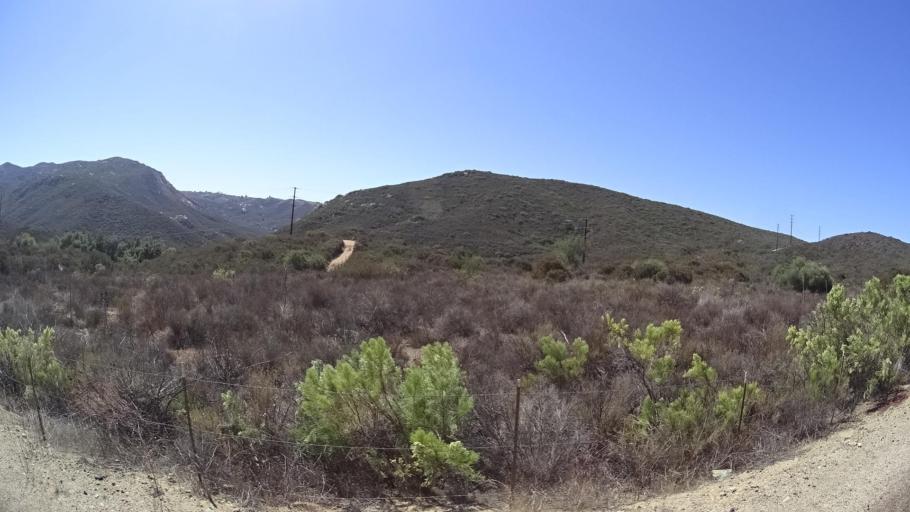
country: US
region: California
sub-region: San Diego County
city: Alpine
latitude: 32.8004
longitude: -116.7617
